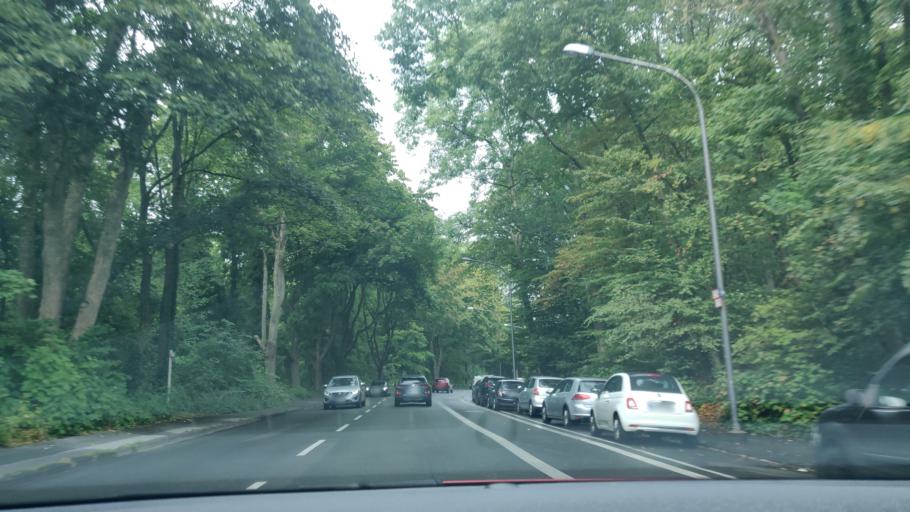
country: DE
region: North Rhine-Westphalia
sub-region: Regierungsbezirk Dusseldorf
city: Wuppertal
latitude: 51.2766
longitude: 7.1225
